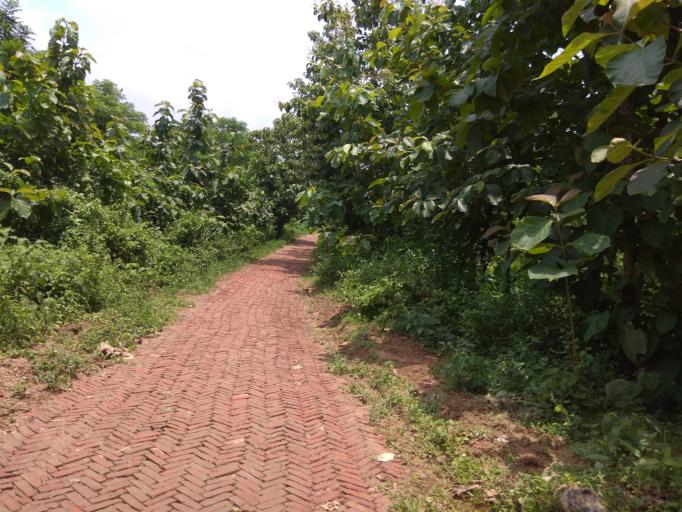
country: BD
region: Chittagong
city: Manikchari
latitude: 22.8841
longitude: 91.9264
